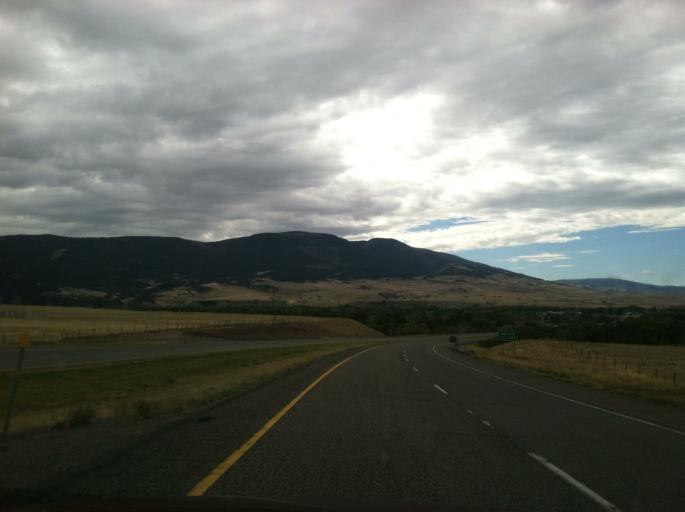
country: US
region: Montana
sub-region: Park County
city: Livingston
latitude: 45.6450
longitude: -110.5538
